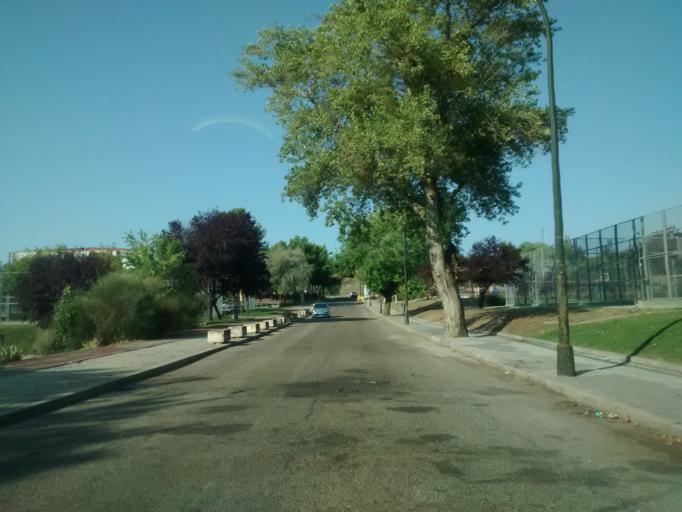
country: ES
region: Madrid
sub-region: Provincia de Madrid
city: Las Tablas
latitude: 40.5477
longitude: -3.6996
